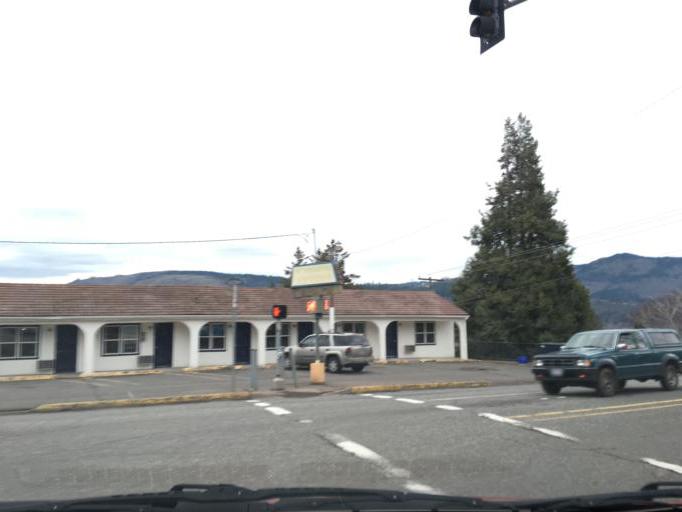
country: US
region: Oregon
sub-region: Hood River County
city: Hood River
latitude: 45.7087
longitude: -121.5251
